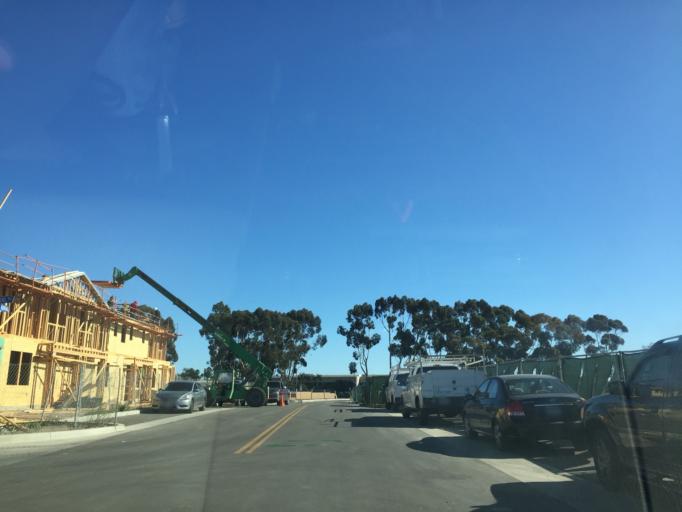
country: US
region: California
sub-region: Santa Barbara County
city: Isla Vista
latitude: 34.4340
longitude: -119.8594
